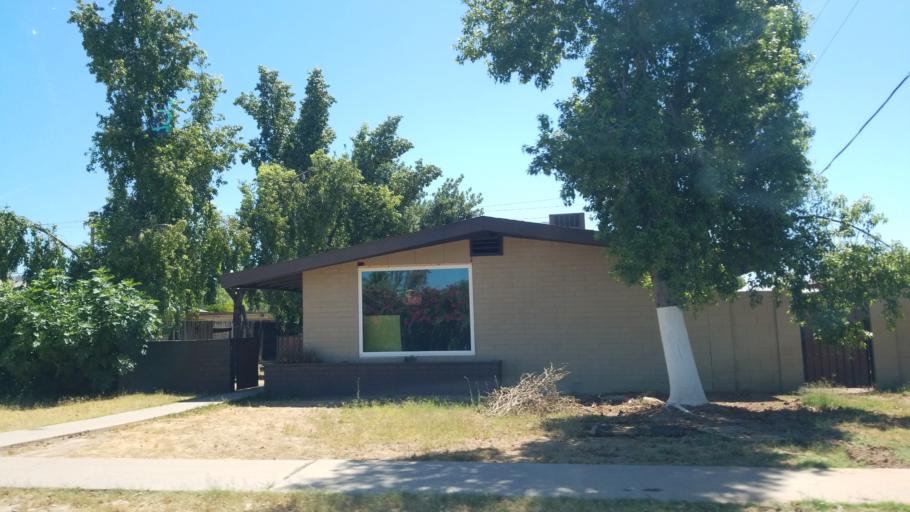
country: US
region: Arizona
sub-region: Maricopa County
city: Phoenix
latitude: 33.5040
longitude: -112.0880
